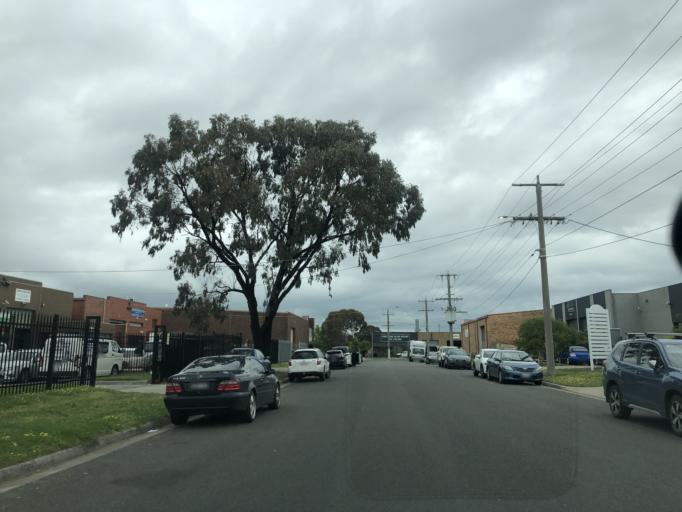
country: AU
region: Victoria
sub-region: Greater Dandenong
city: Dandenong
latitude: -37.9816
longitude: 145.1900
